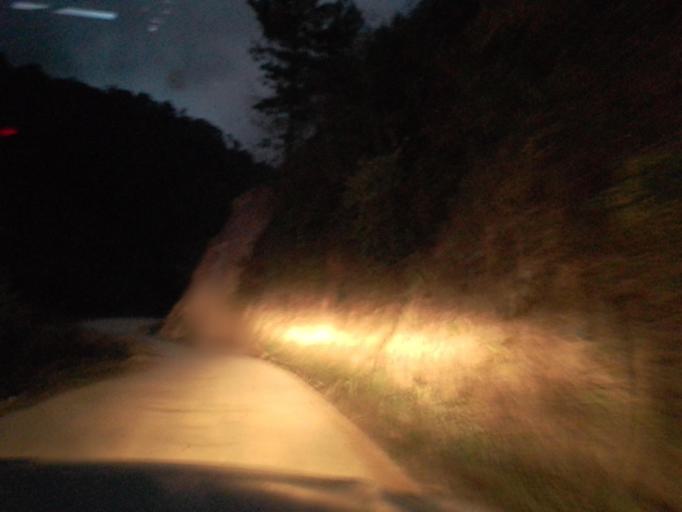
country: GT
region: San Marcos
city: Tacana
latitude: 15.2340
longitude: -92.1981
